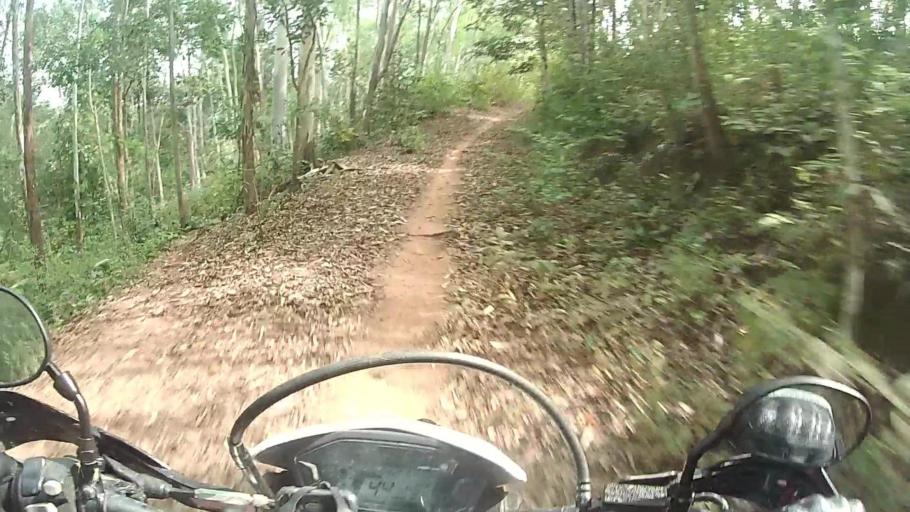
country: TH
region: Chiang Mai
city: Mae On
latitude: 18.7262
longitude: 99.2885
